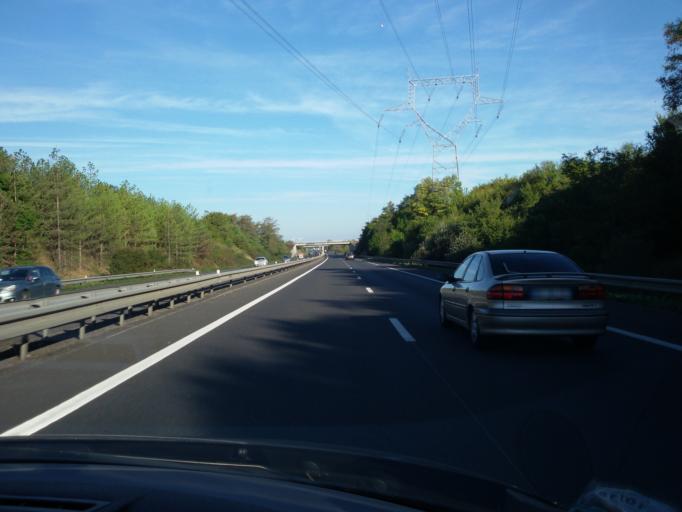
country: FR
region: Centre
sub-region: Departement du Cher
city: La Chapelle-Saint-Ursin
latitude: 47.0566
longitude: 2.3107
